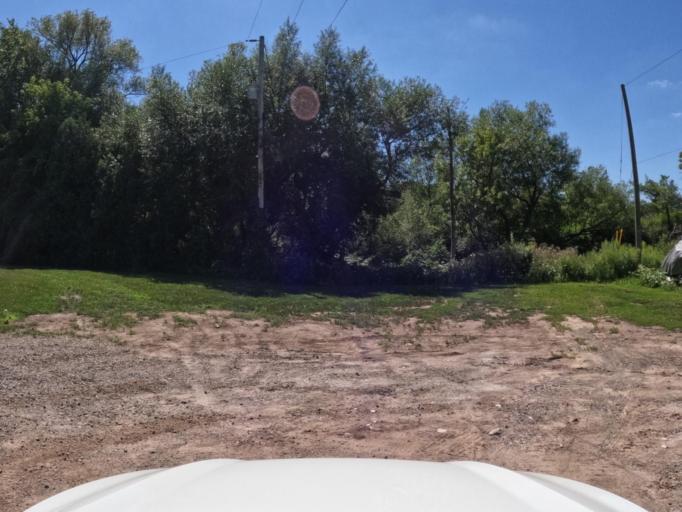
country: CA
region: Ontario
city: Cambridge
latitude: 43.4118
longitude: -80.2605
